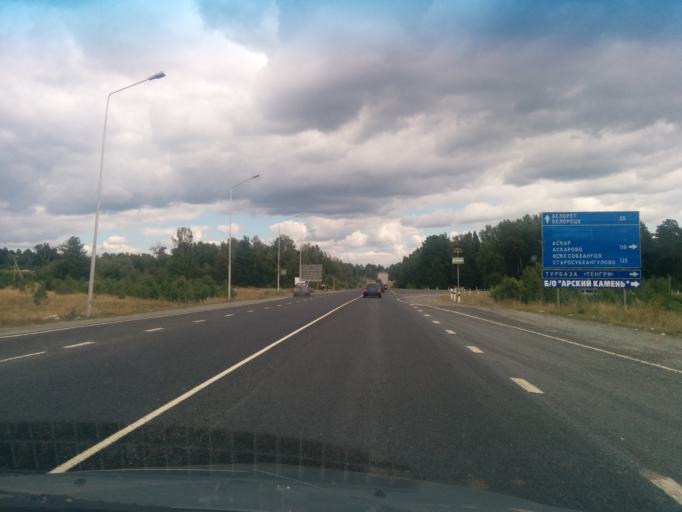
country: RU
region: Bashkortostan
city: Lomovka
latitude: 53.8977
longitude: 58.0810
